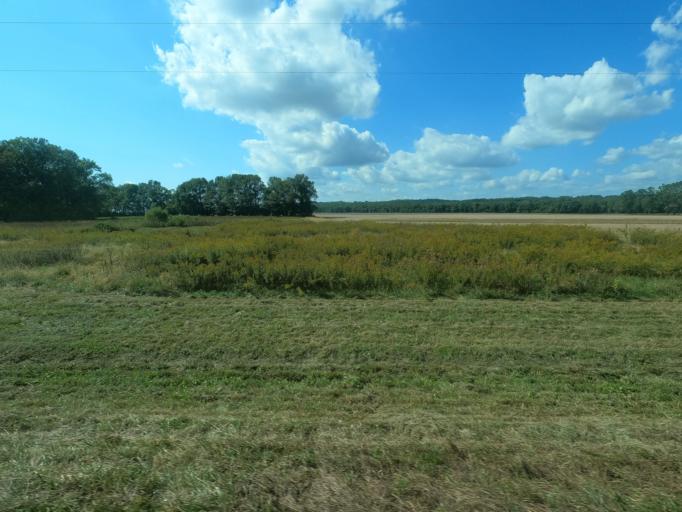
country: US
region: Illinois
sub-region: Massac County
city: Metropolis
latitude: 37.2890
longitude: -88.7567
